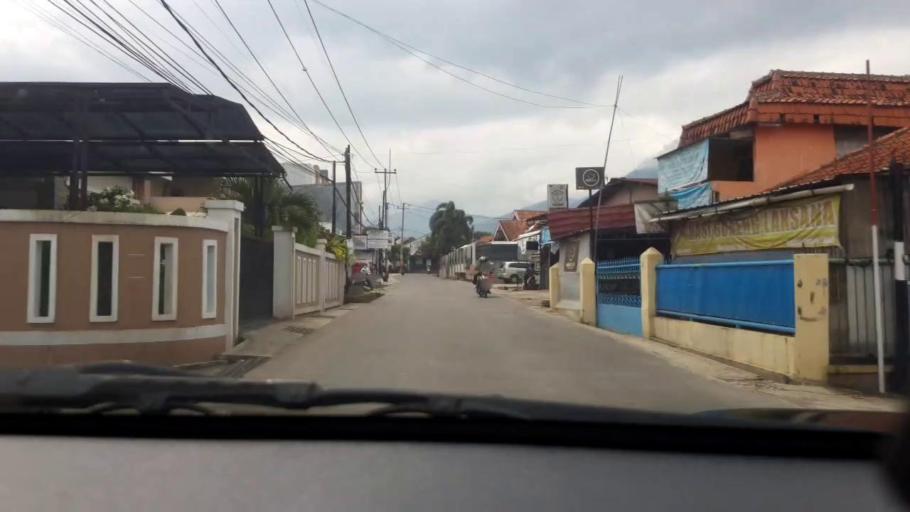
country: ID
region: West Java
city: Cileunyi
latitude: -6.9384
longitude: 107.7262
